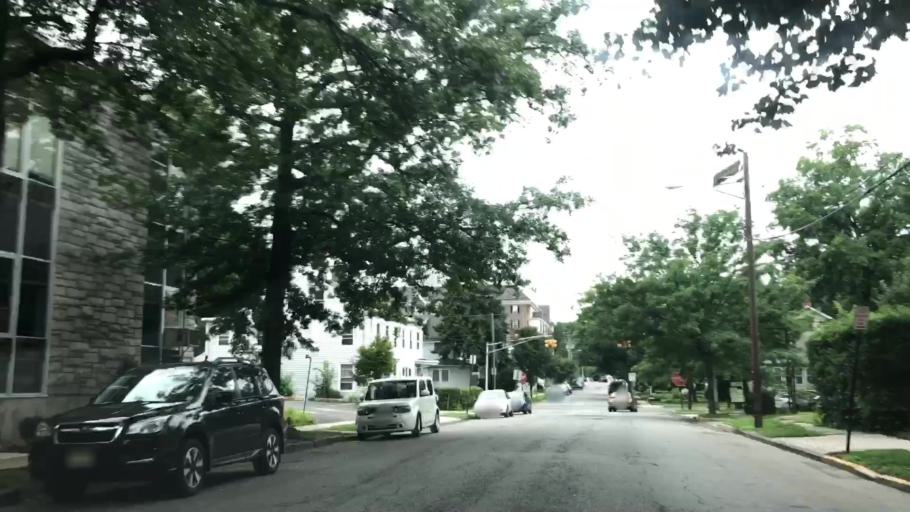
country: US
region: New Jersey
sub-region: Essex County
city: Glen Ridge
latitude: 40.7979
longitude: -74.1977
